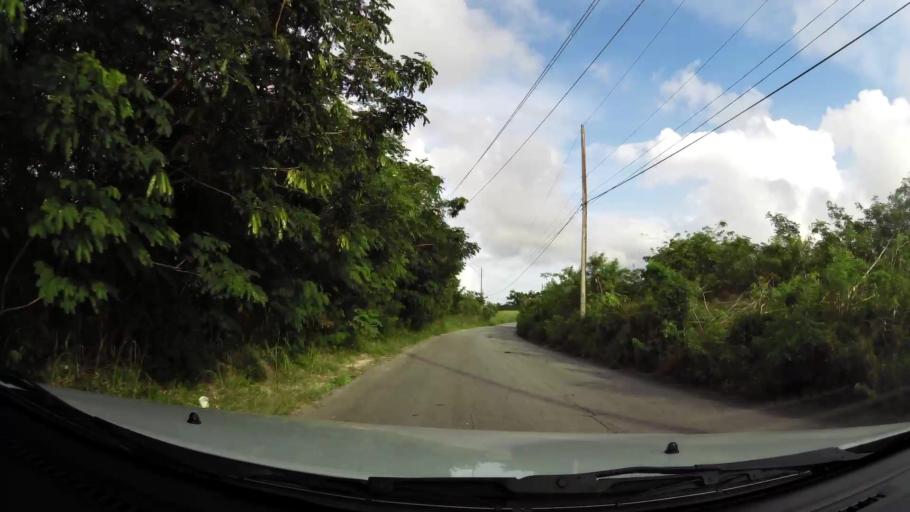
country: BB
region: Christ Church
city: Oistins
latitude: 13.0943
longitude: -59.5550
